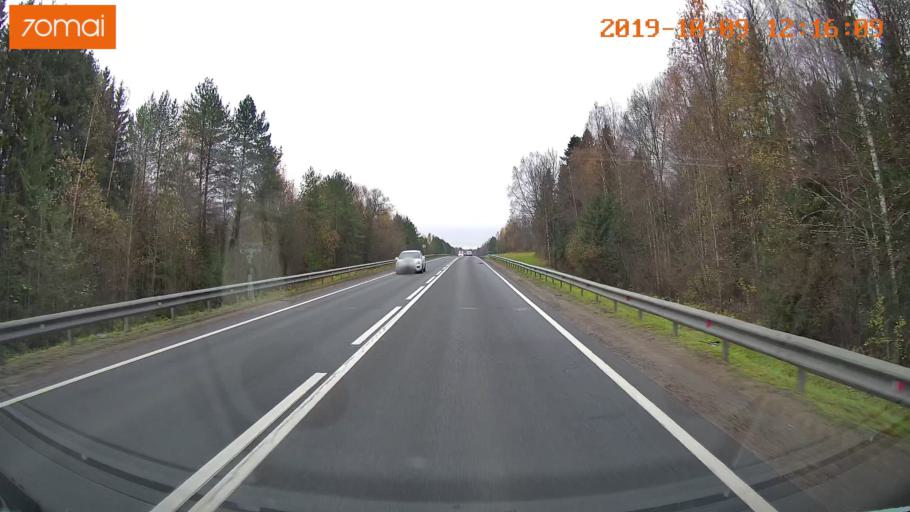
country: RU
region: Jaroslavl
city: Prechistoye
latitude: 58.4727
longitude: 40.3217
